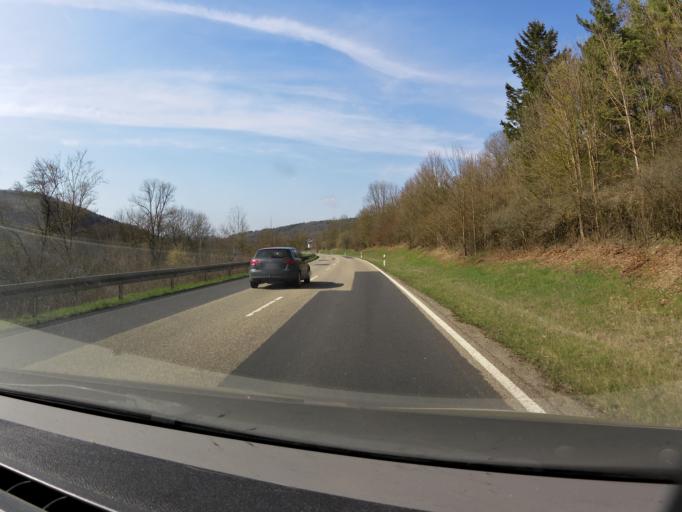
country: DE
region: Baden-Wuerttemberg
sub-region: Regierungsbezirk Stuttgart
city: Creglingen
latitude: 49.4584
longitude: 10.0617
